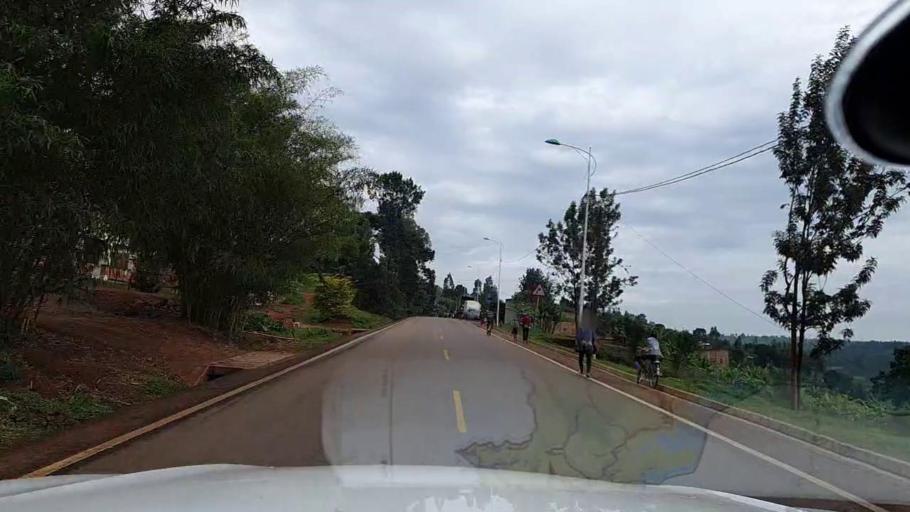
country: RW
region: Southern Province
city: Butare
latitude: -2.5806
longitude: 29.7353
